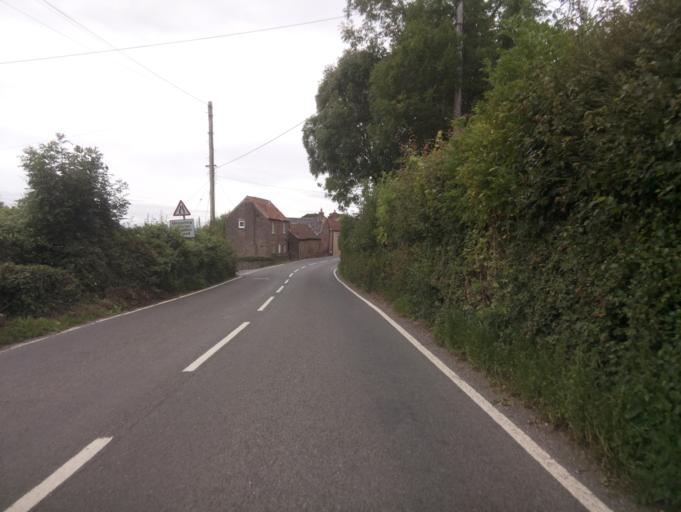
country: GB
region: England
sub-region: Somerset
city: Bradley Cross
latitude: 51.2532
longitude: -2.7480
